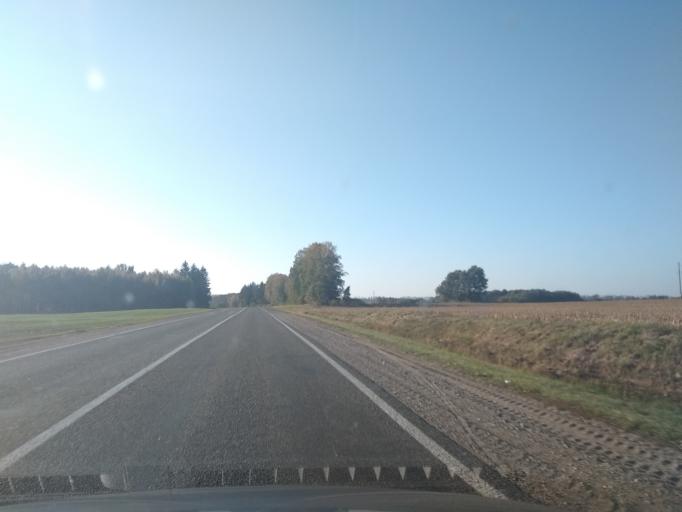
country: BY
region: Grodnenskaya
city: Vyalikaya Byerastavitsa
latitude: 53.1180
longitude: 24.0499
